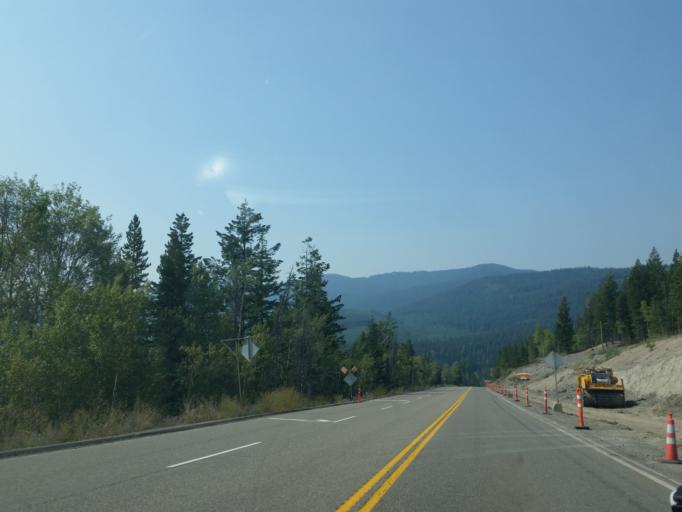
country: CA
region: British Columbia
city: Princeton
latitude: 49.2735
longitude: -120.5768
